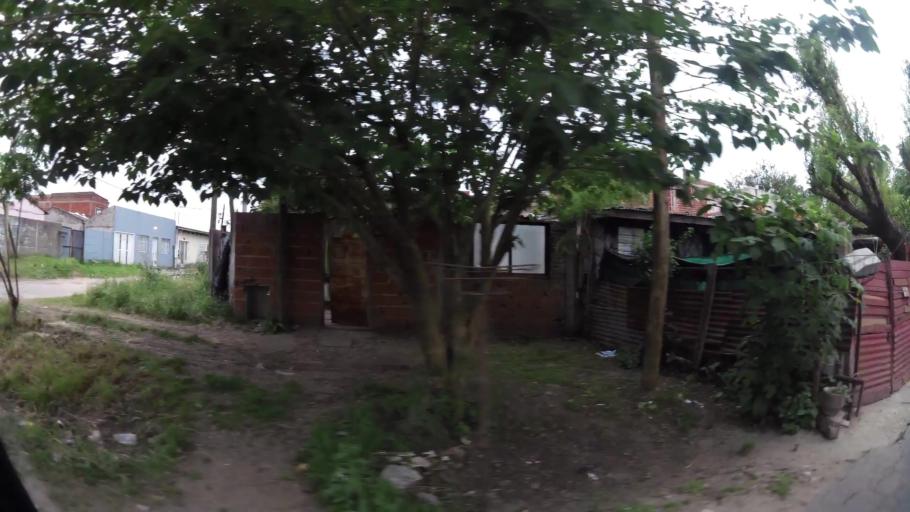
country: AR
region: Buenos Aires
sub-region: Partido de La Plata
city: La Plata
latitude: -34.9294
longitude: -57.9929
